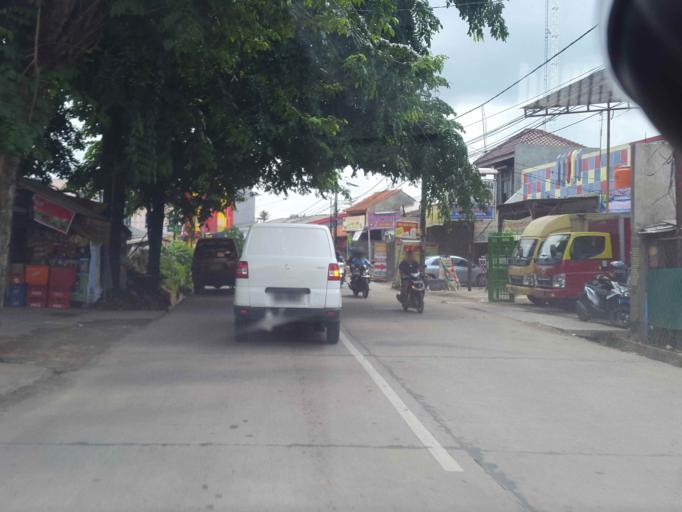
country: ID
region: West Java
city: Bekasi
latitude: -6.2934
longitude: 106.9655
